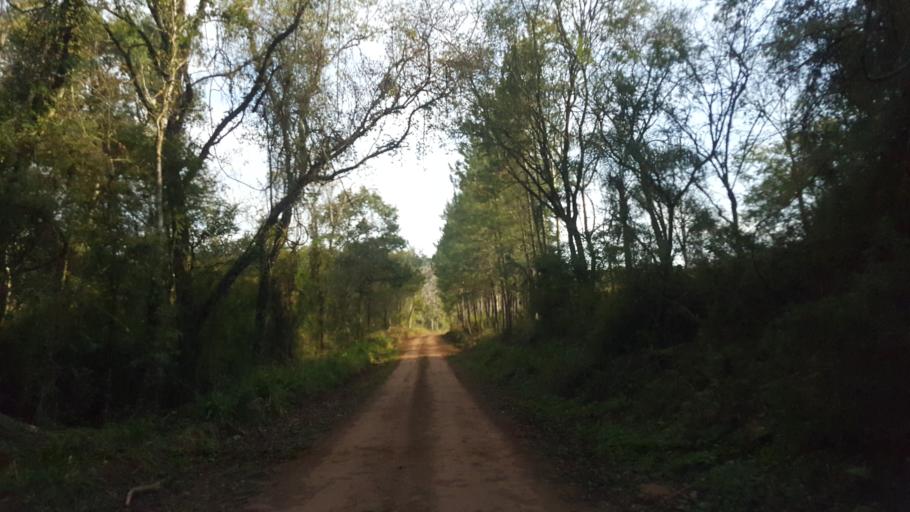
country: AR
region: Misiones
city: Capiovi
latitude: -26.8988
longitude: -55.0922
